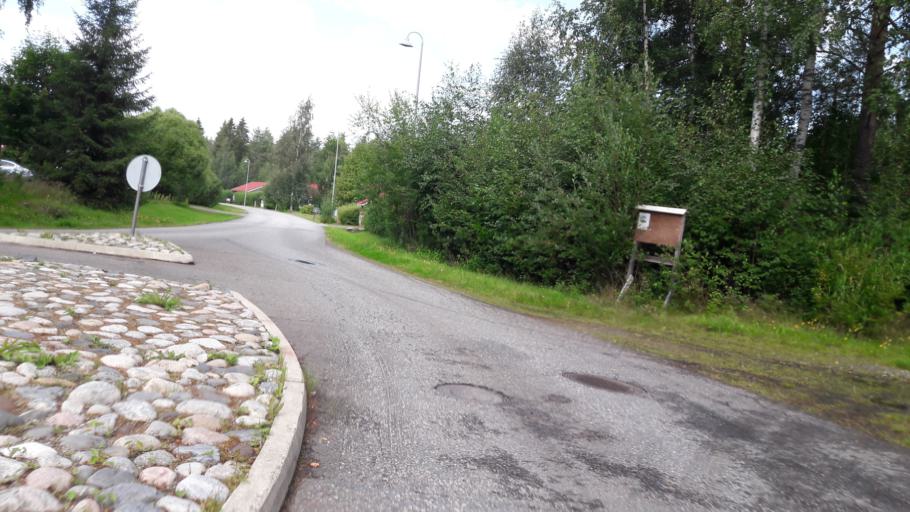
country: FI
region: North Karelia
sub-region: Joensuu
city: Joensuu
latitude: 62.5097
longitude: 29.8299
